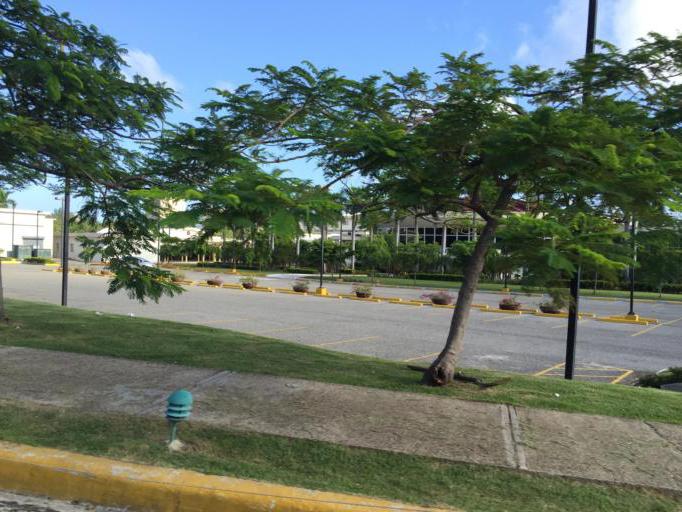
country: DO
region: Nacional
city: La Julia
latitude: 18.4606
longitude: -69.9203
